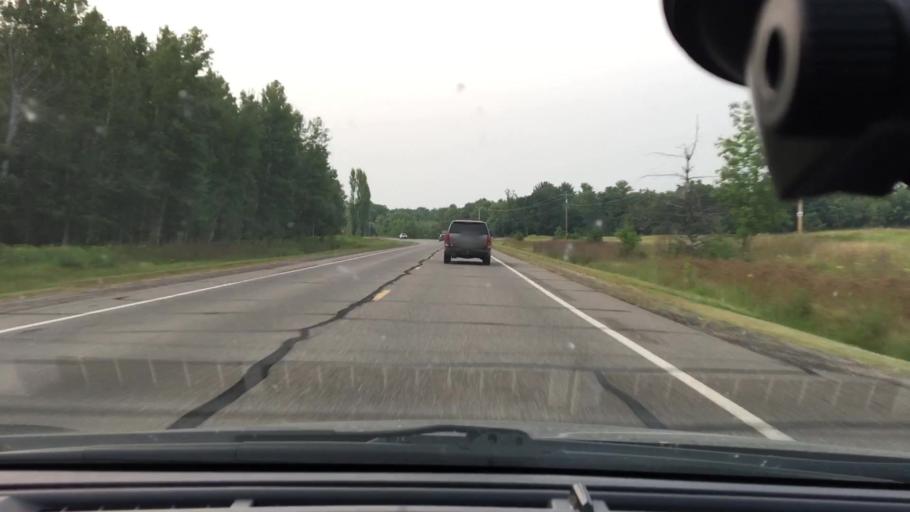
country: US
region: Minnesota
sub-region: Crow Wing County
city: Crosby
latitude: 46.4656
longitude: -93.8866
